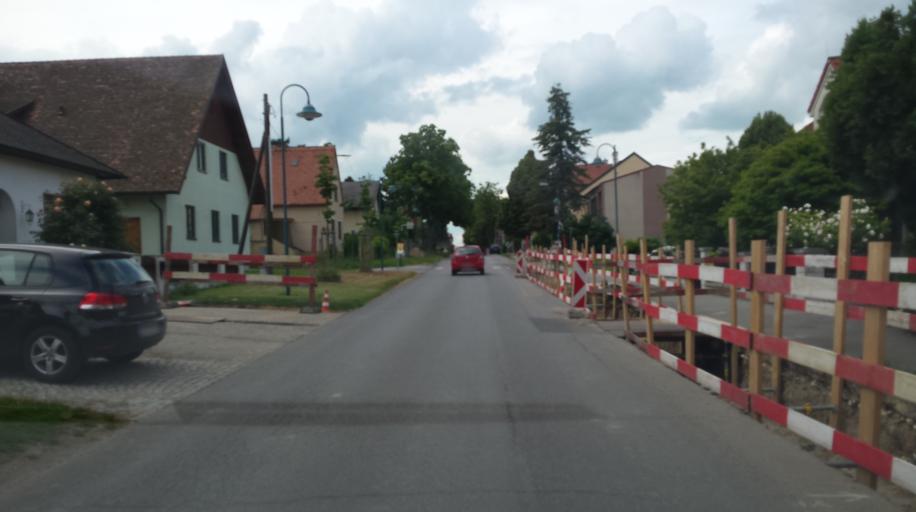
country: AT
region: Lower Austria
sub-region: Politischer Bezirk Mistelbach
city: Wolkersdorf im Weinviertel
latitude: 48.3775
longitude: 16.5174
